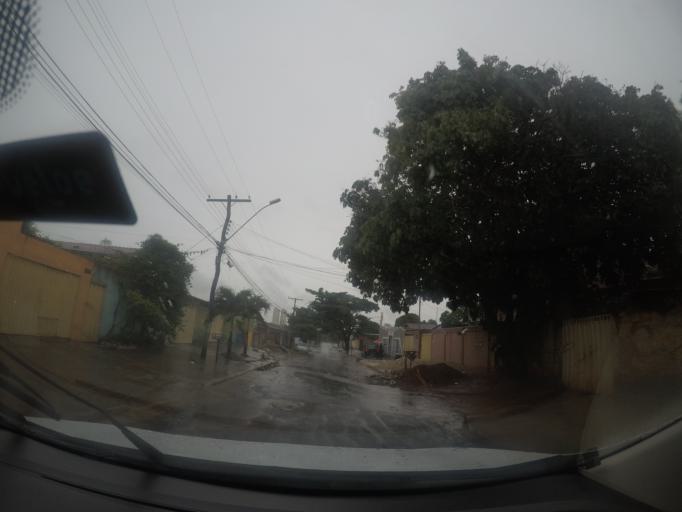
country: BR
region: Goias
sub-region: Goiania
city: Goiania
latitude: -16.6536
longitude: -49.3120
